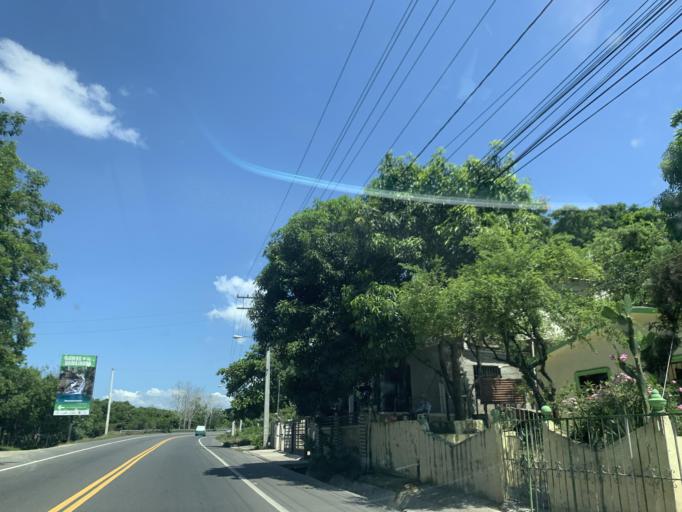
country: DO
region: Puerto Plata
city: Imbert
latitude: 19.7331
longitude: -70.8317
